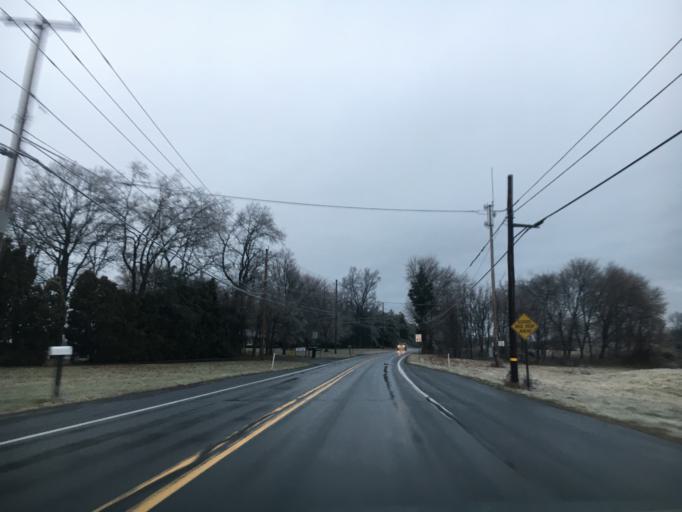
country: US
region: Pennsylvania
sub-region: Lehigh County
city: Schnecksville
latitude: 40.6278
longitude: -75.6174
